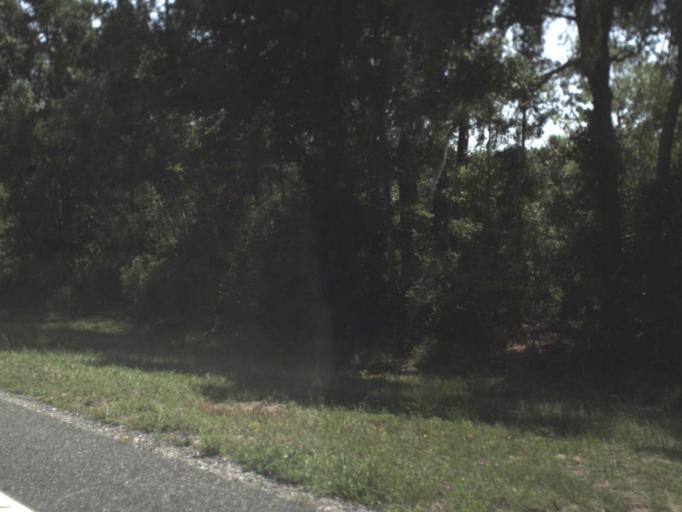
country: US
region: Florida
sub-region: Levy County
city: Inglis
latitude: 29.1034
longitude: -82.6363
